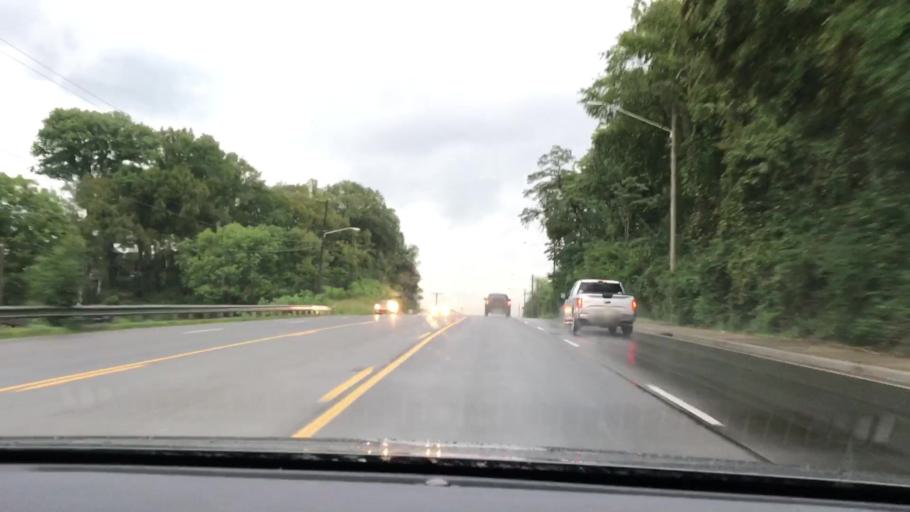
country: US
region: Tennessee
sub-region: Davidson County
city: Oak Hill
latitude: 36.0830
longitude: -86.7092
